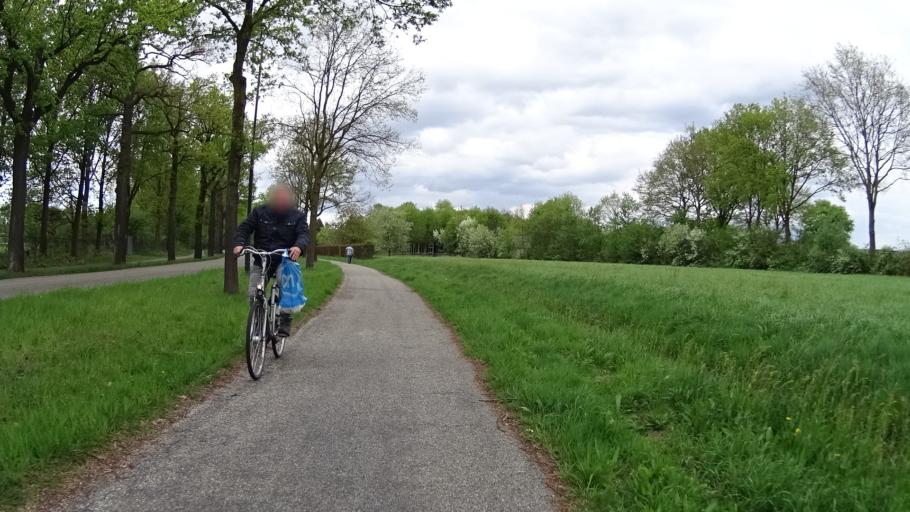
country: NL
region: North Brabant
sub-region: Gemeente Boekel
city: Boekel
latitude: 51.5610
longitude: 5.7005
